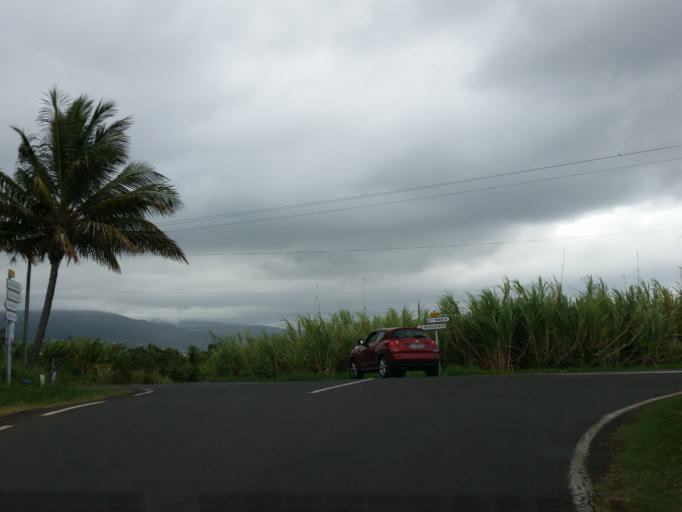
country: RE
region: Reunion
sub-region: Reunion
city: Sainte-Marie
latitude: -20.9268
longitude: 55.5370
